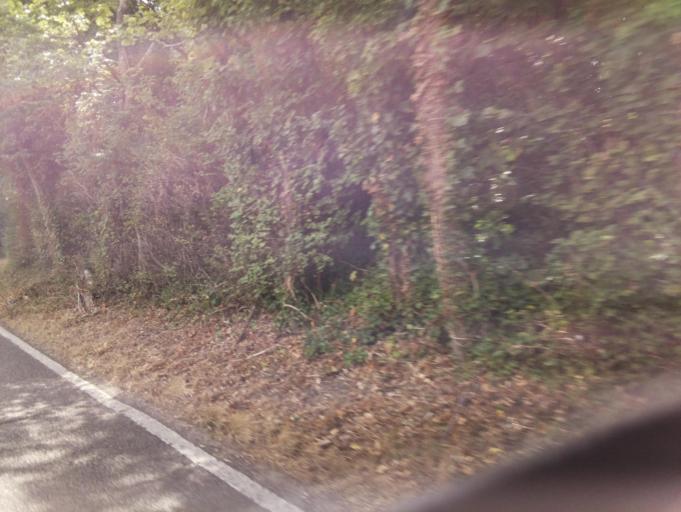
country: GB
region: England
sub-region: Surrey
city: Chilworth
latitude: 51.2421
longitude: -0.5241
